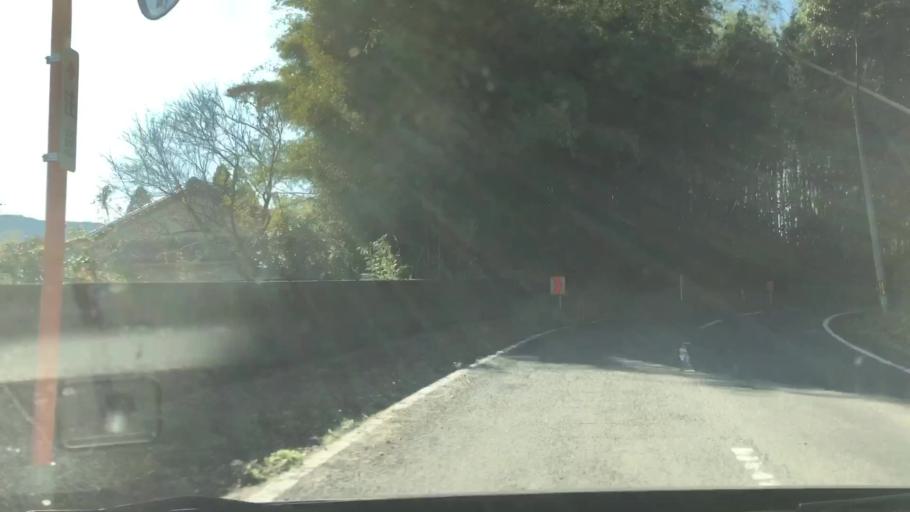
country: JP
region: Kagoshima
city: Satsumasendai
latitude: 31.8549
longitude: 130.3622
